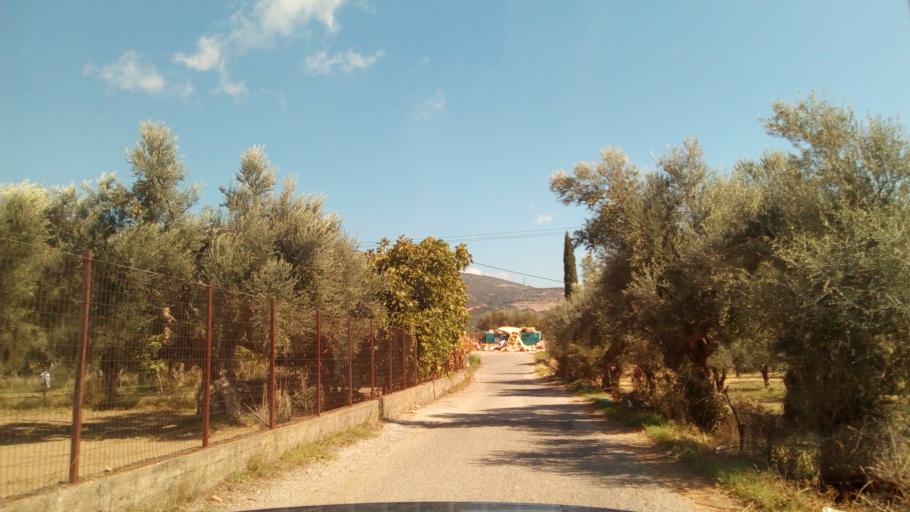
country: GR
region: West Greece
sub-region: Nomos Aitolias kai Akarnanias
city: Nafpaktos
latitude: 38.3907
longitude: 21.7980
